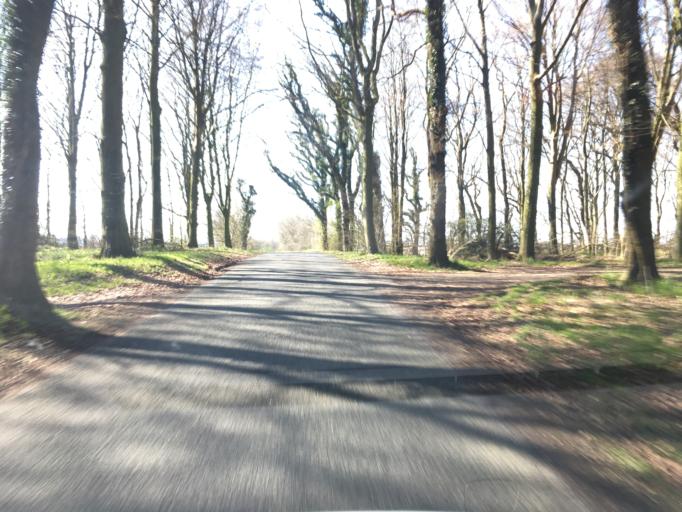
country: DK
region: South Denmark
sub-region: Aabenraa Kommune
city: Krusa
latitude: 54.9271
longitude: 9.4248
